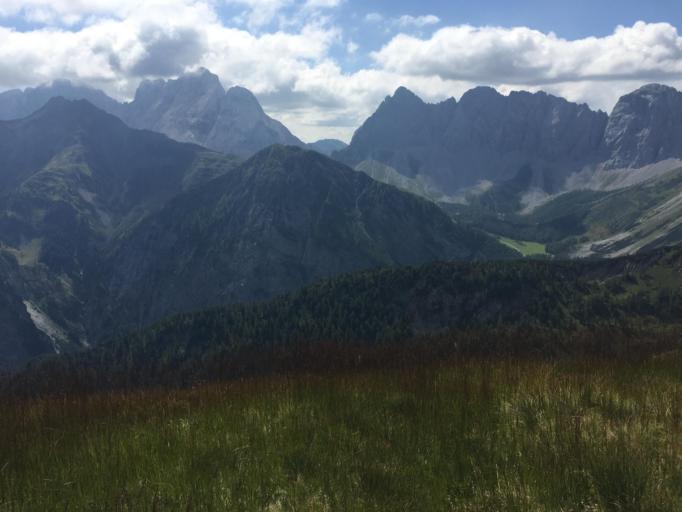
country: IT
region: Friuli Venezia Giulia
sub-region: Provincia di Udine
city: Forni Avoltri
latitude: 46.6444
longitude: 12.8437
